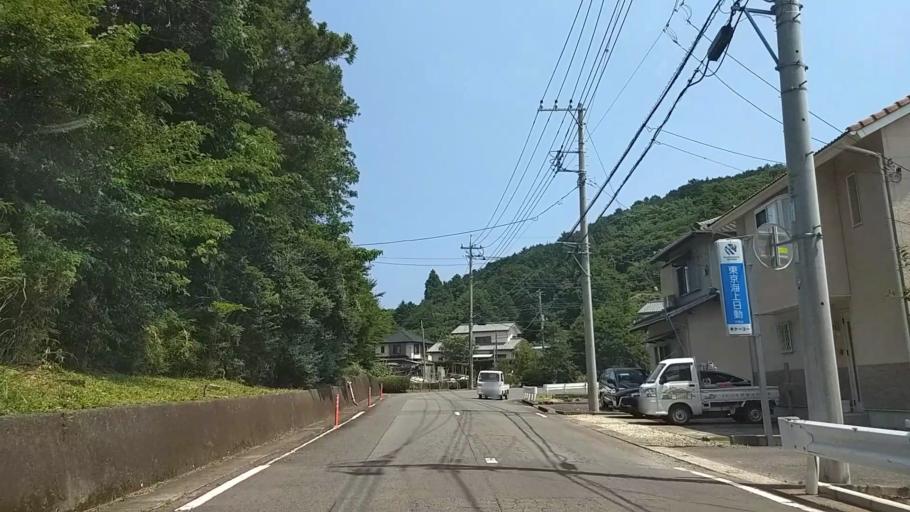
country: JP
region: Shizuoka
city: Ito
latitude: 34.9444
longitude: 139.1110
